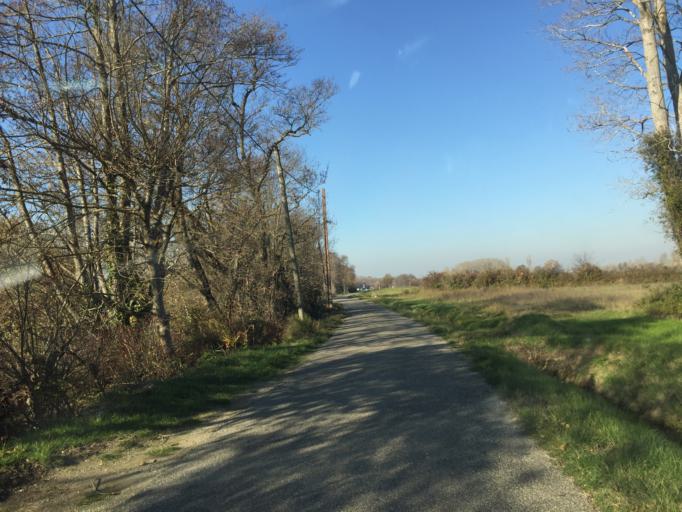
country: FR
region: Provence-Alpes-Cote d'Azur
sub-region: Departement du Vaucluse
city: Entraigues-sur-la-Sorgue
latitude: 44.0176
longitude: 4.9209
